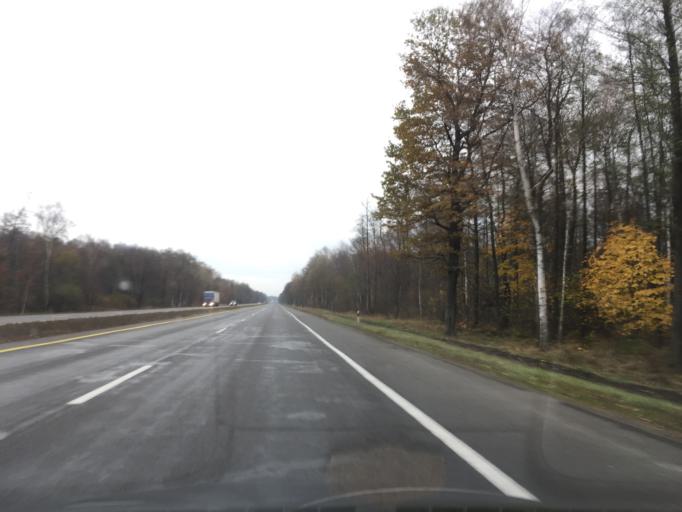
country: BY
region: Gomel
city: Horad Rechytsa
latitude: 52.3500
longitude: 30.5902
